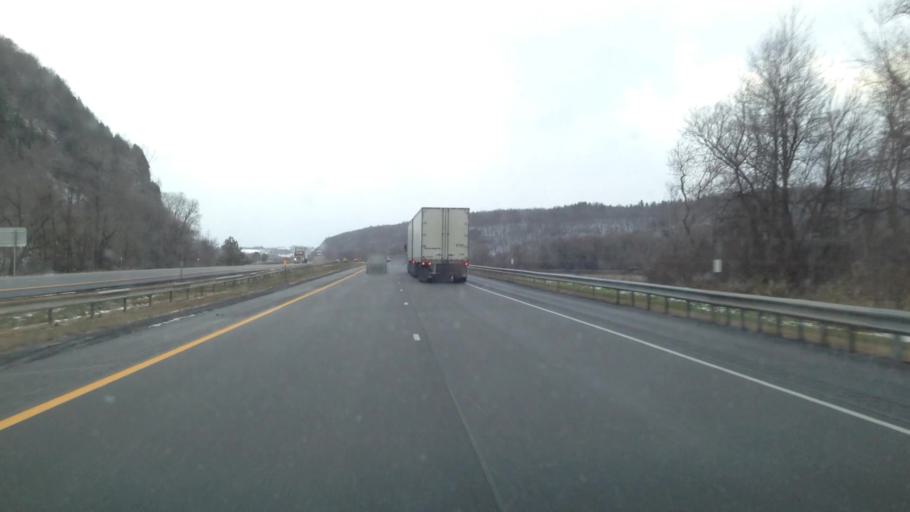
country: US
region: New York
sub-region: Montgomery County
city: Canajoharie
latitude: 42.8959
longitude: -74.4773
